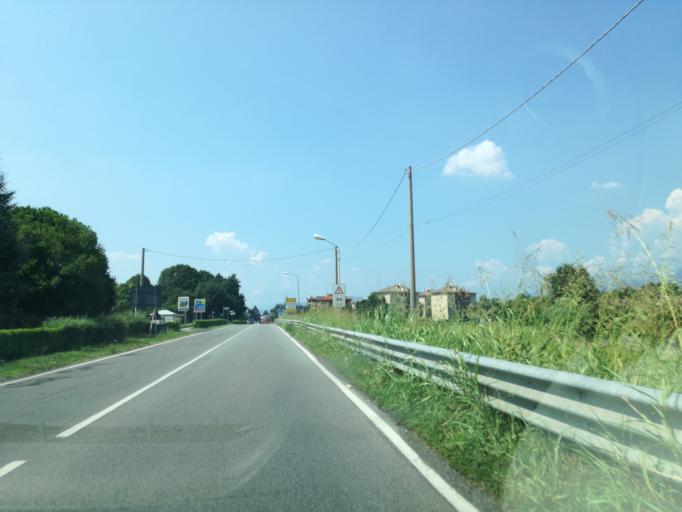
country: IT
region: Lombardy
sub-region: Provincia di Monza e Brianza
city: Cornate d'Adda
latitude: 45.6407
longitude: 9.4694
